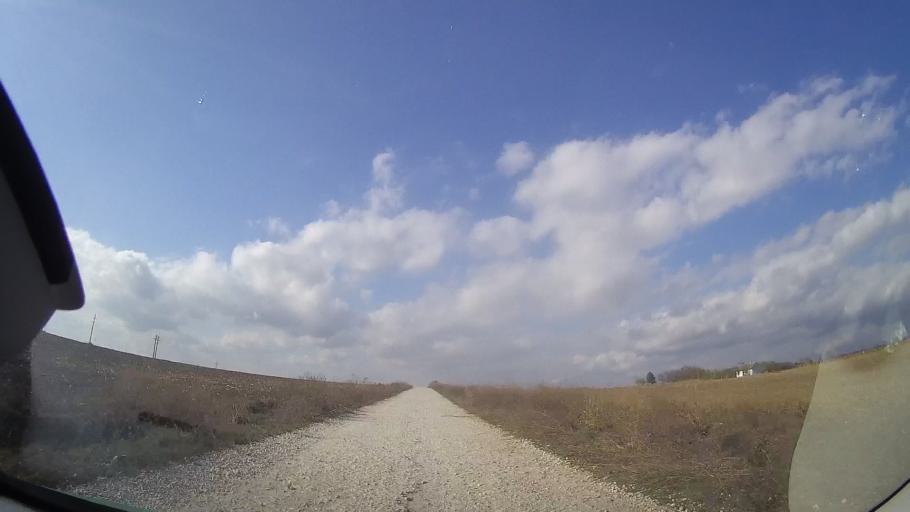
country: RO
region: Constanta
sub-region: Comuna Douazeci si Trei August
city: Douazeci si Trei August
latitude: 43.9107
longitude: 28.5983
